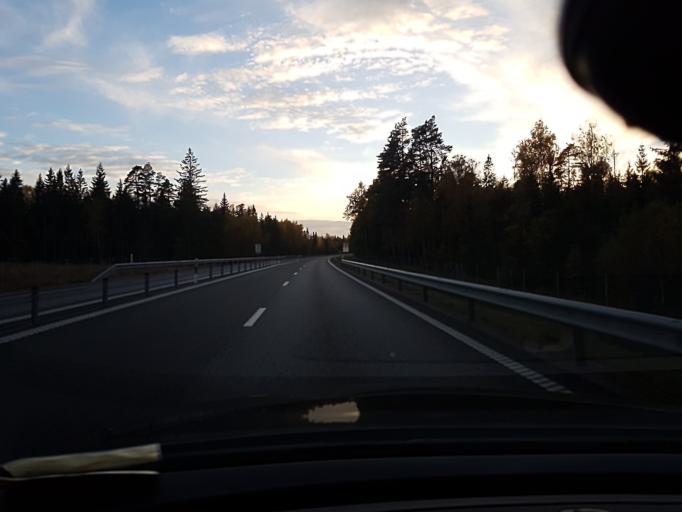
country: SE
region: Kronoberg
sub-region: Ljungby Kommun
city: Ljungby
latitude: 56.7940
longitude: 13.8499
